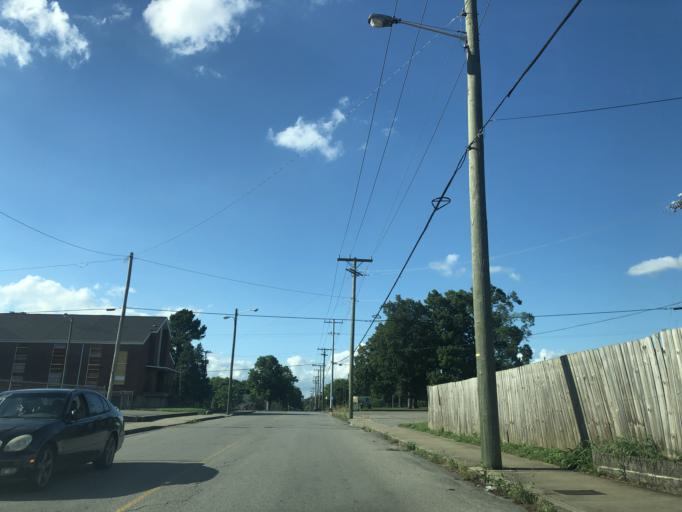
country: US
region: Tennessee
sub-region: Davidson County
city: Nashville
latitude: 36.1803
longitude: -86.7690
